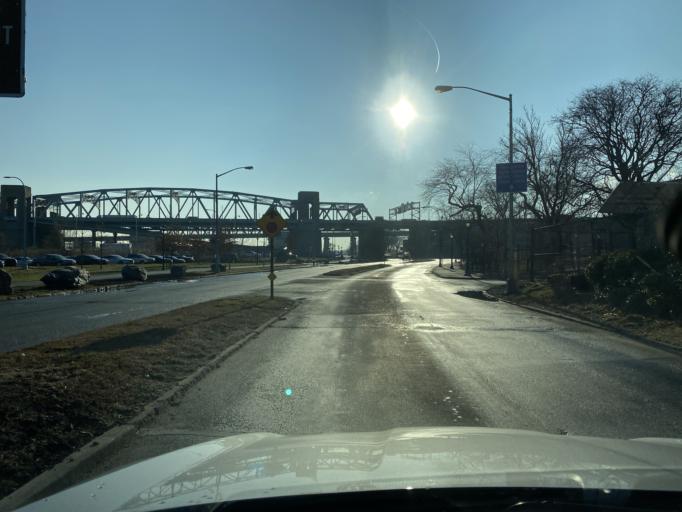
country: US
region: New York
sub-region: New York County
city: Manhattan
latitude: 40.7994
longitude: -73.9221
